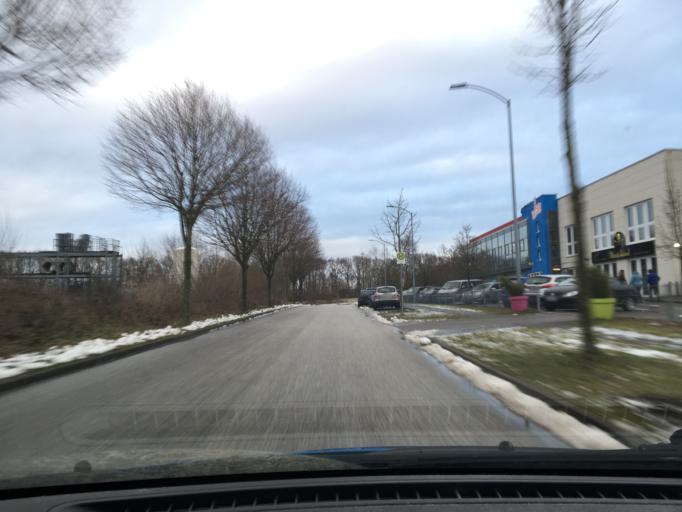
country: DE
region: Schleswig-Holstein
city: Ottenbuttel
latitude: 53.9578
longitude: 9.4971
